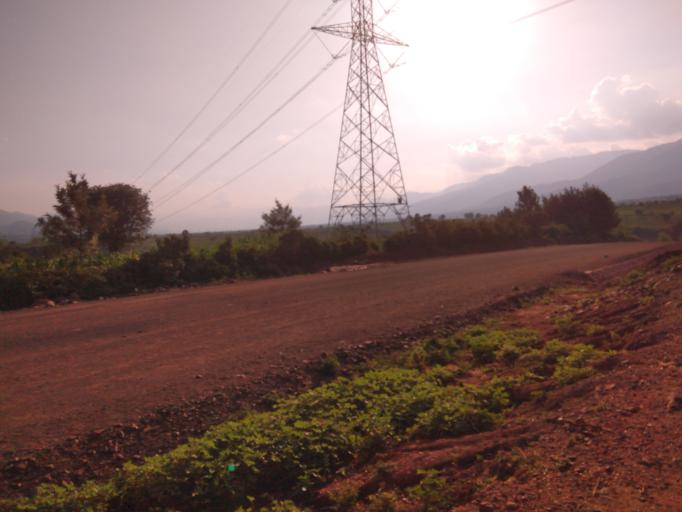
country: ET
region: Southern Nations, Nationalities, and People's Region
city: Felege Neway
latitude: 6.3925
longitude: 37.0327
